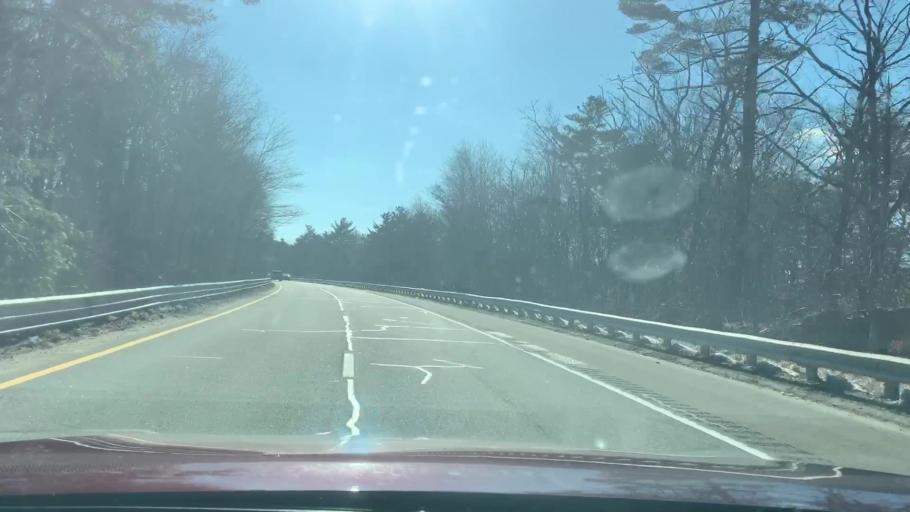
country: US
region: Massachusetts
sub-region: Essex County
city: Essex
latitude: 42.6112
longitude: -70.7353
